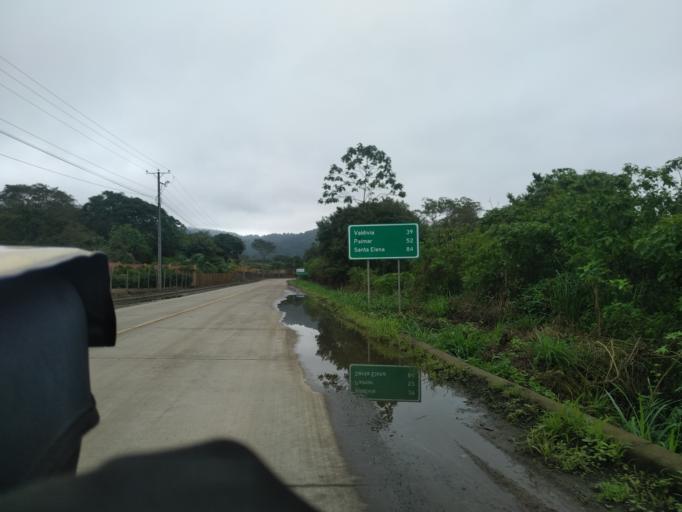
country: EC
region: Manabi
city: Jipijapa
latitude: -1.6689
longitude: -80.8094
